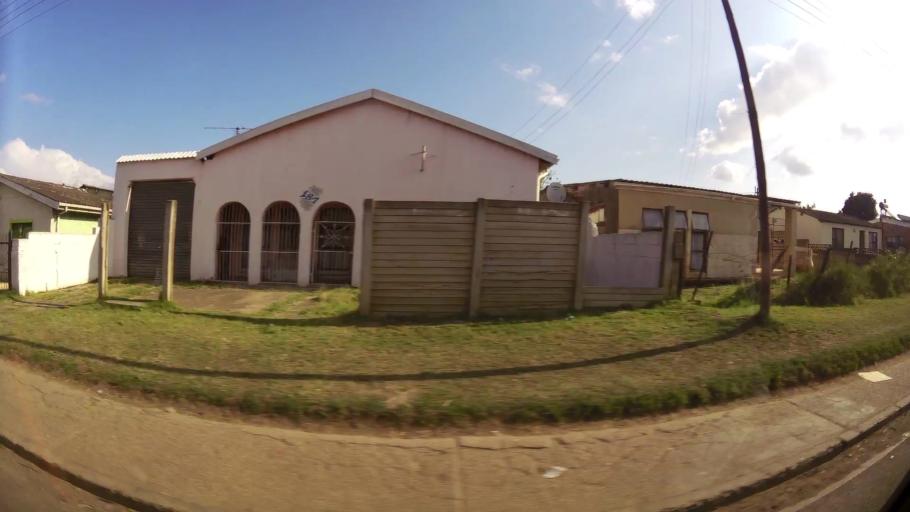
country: ZA
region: Eastern Cape
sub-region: Nelson Mandela Bay Metropolitan Municipality
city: Uitenhage
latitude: -33.7367
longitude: 25.3703
